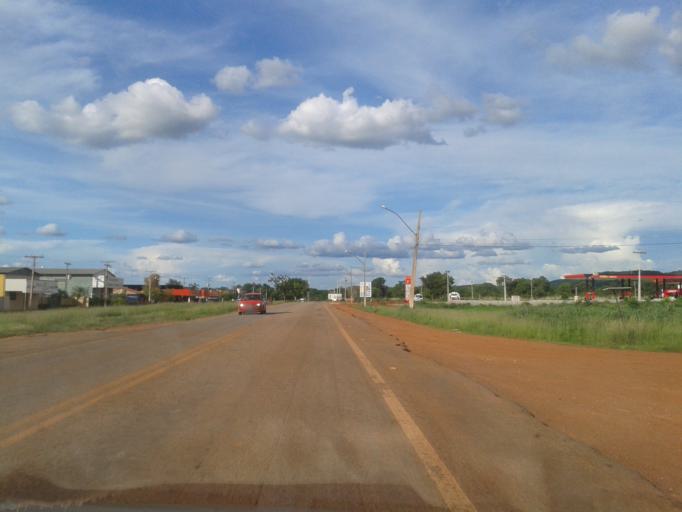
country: BR
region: Goias
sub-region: Crixas
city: Crixas
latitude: -14.1119
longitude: -50.3428
